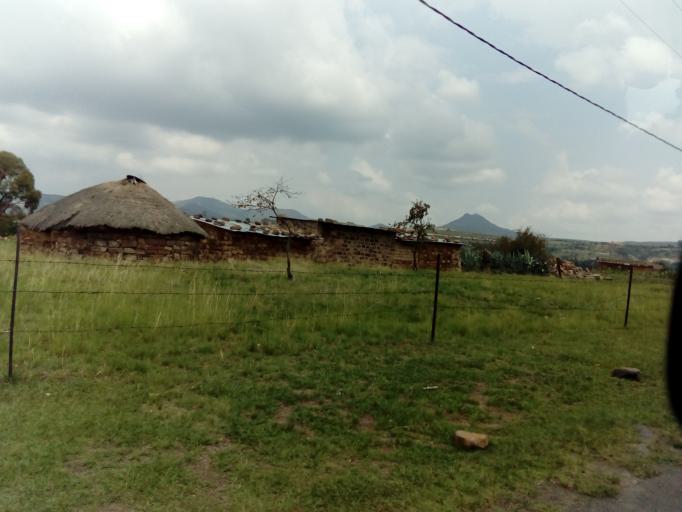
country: LS
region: Leribe
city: Leribe
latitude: -29.0159
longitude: 28.0011
